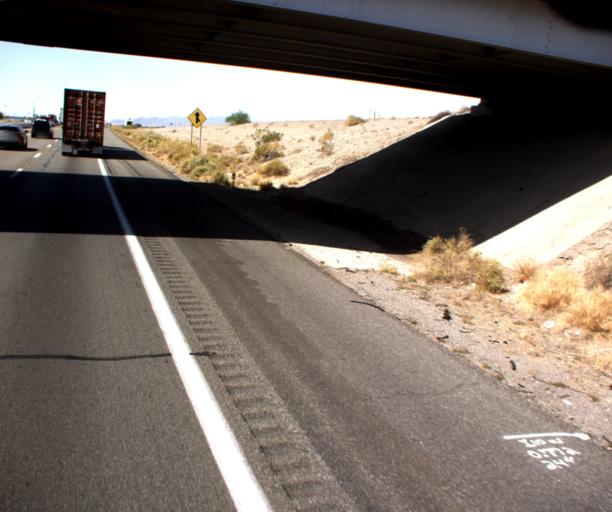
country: US
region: Arizona
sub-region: La Paz County
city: Ehrenberg
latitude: 33.6026
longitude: -114.5186
